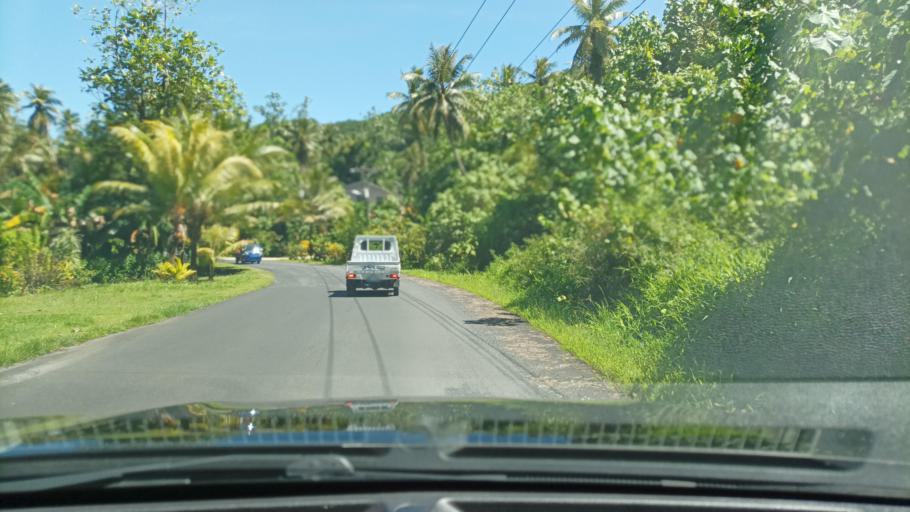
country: FM
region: Pohnpei
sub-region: Madolenihm Municipality
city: Madolenihm Municipality Government
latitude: 6.9166
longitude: 158.3206
